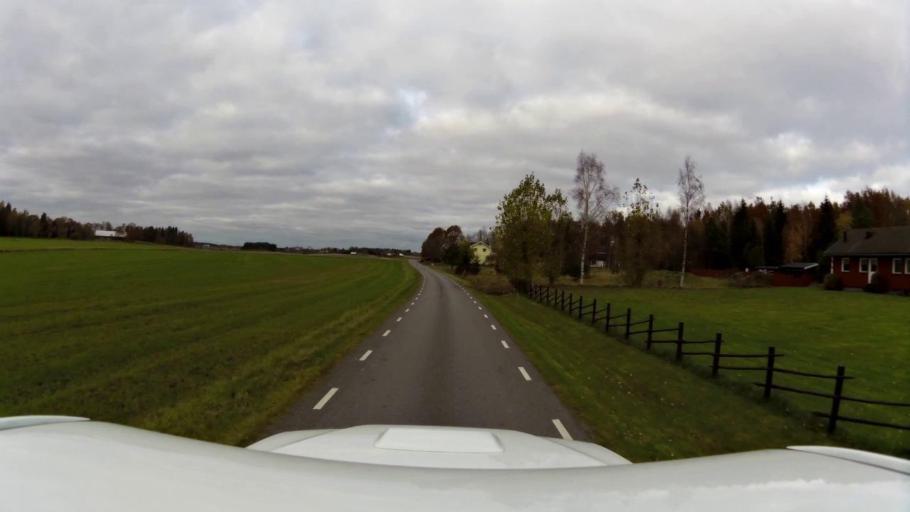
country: SE
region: OEstergoetland
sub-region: Linkopings Kommun
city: Linghem
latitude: 58.3929
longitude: 15.8011
